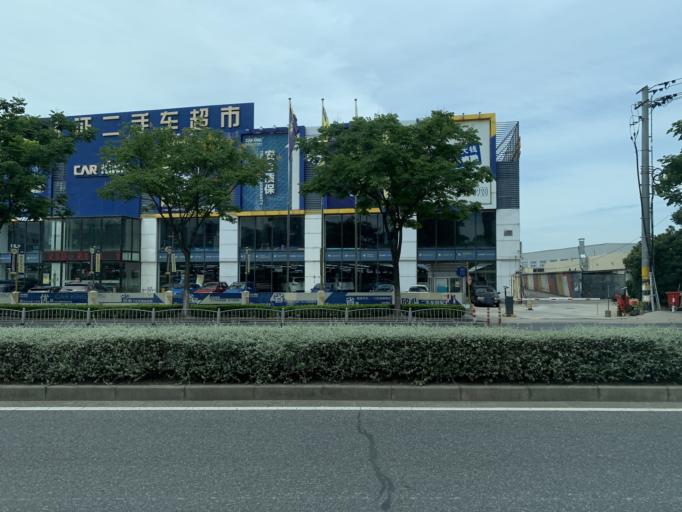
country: CN
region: Shanghai Shi
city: Kangqiao
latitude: 31.1575
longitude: 121.5603
